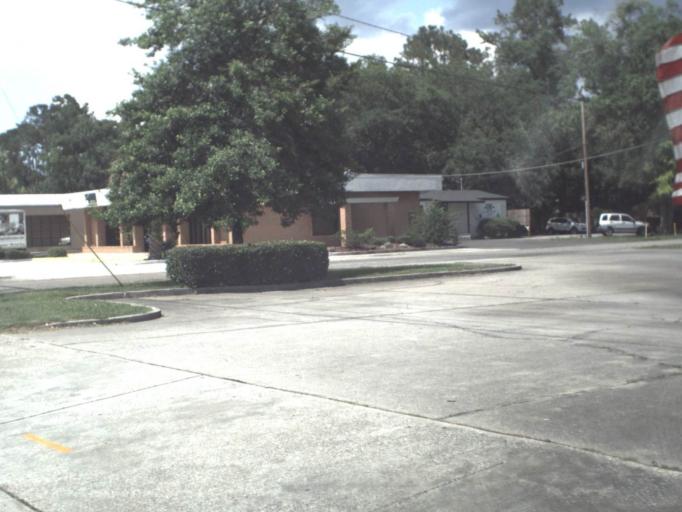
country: US
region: Florida
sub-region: Clay County
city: Orange Park
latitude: 30.1727
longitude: -81.7012
